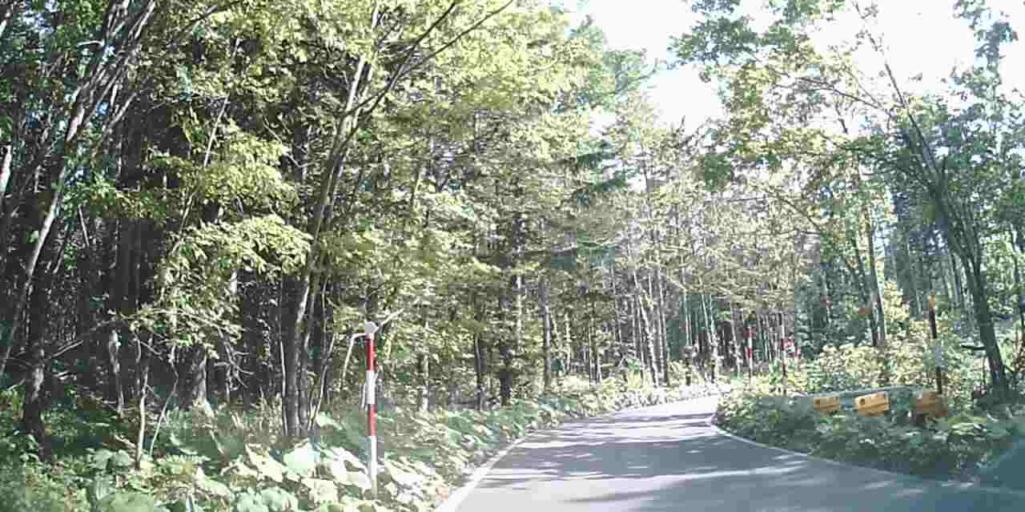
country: JP
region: Hokkaido
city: Shiraoi
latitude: 42.7415
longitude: 141.4112
